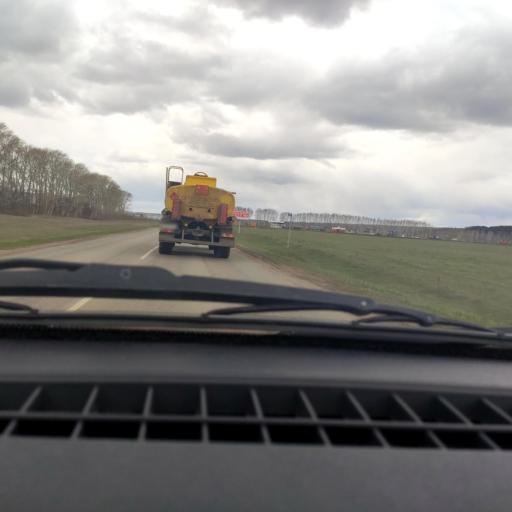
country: RU
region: Bashkortostan
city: Chekmagush
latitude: 55.1285
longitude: 54.6922
